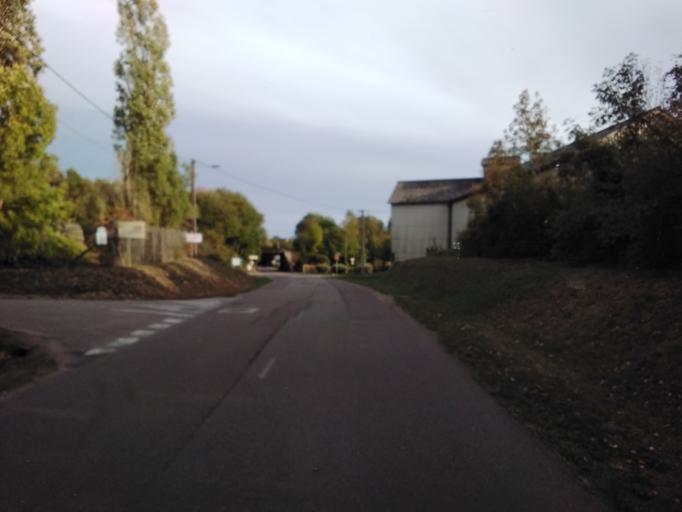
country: FR
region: Champagne-Ardenne
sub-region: Departement de l'Aube
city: Les Riceys
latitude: 47.8497
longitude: 4.3614
